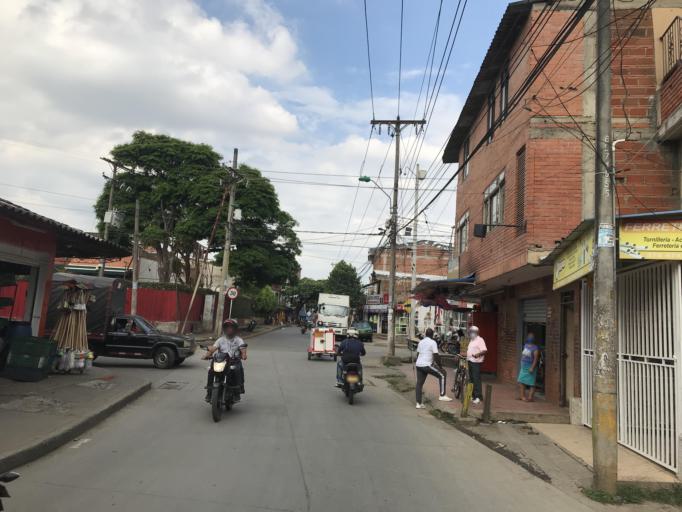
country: CO
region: Valle del Cauca
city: Cali
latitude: 3.3740
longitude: -76.5492
